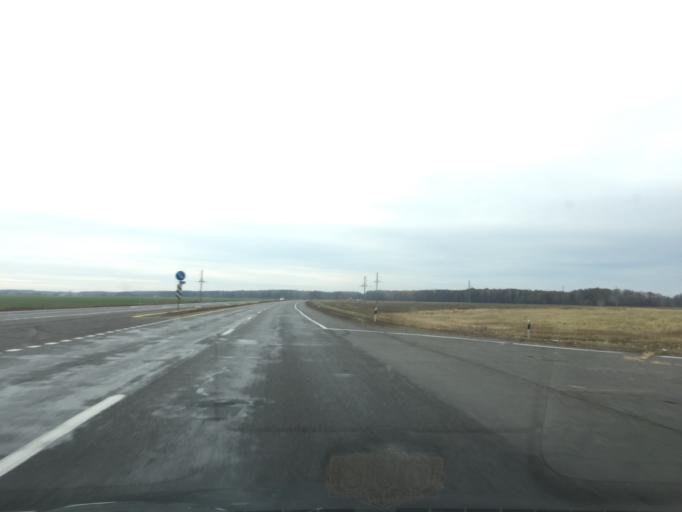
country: BY
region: Gomel
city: Horad Rechytsa
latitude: 52.3426
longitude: 30.5610
